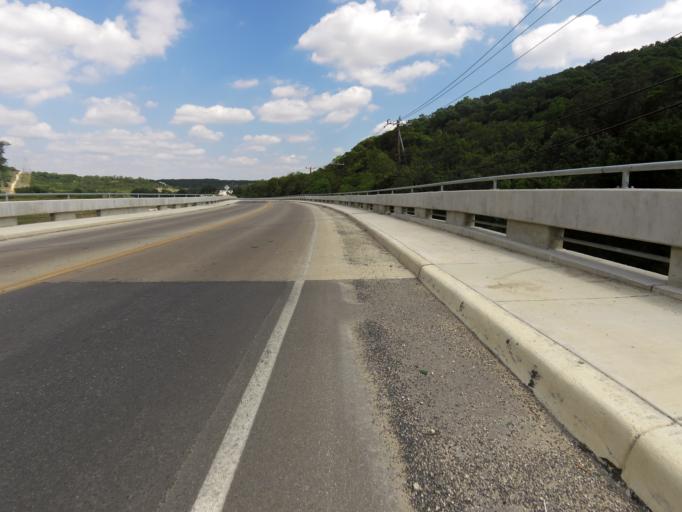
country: US
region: Texas
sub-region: Bexar County
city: Cross Mountain
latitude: 29.6134
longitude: -98.6343
